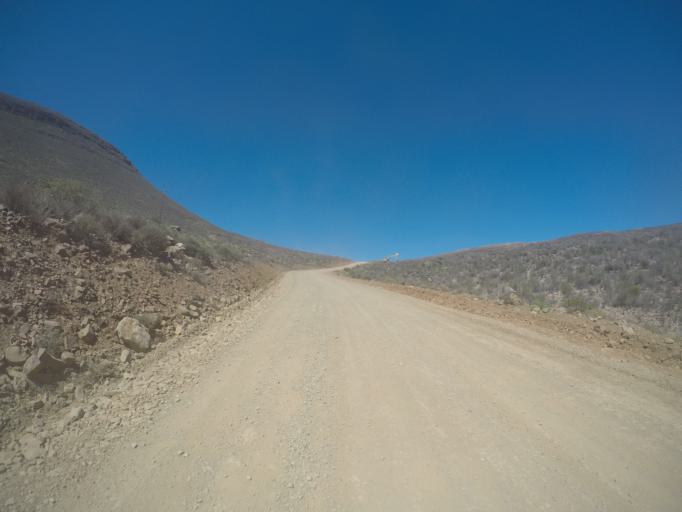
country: ZA
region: Western Cape
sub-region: West Coast District Municipality
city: Clanwilliam
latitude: -32.6052
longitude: 19.3682
